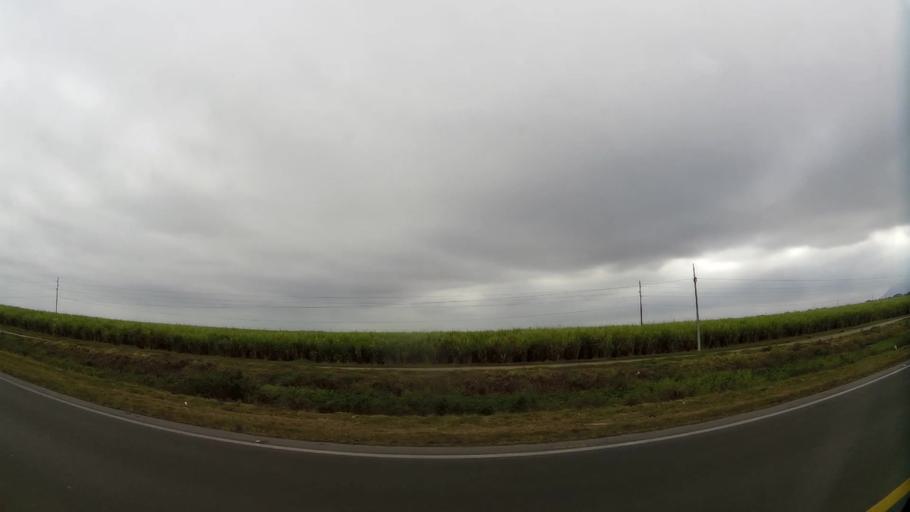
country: EC
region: Guayas
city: Coronel Marcelino Mariduena
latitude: -2.3379
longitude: -79.6352
